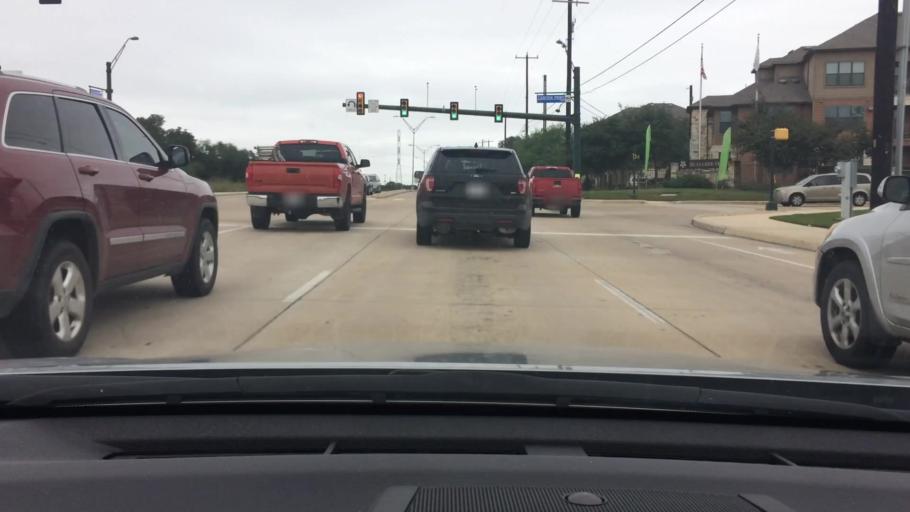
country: US
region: Texas
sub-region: Bexar County
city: Hollywood Park
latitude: 29.6306
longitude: -98.4232
